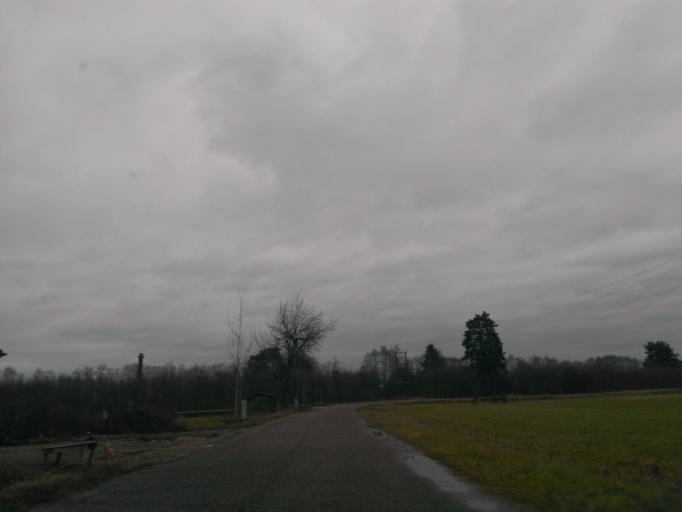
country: LV
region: Adazi
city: Adazi
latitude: 57.0638
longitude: 24.3570
